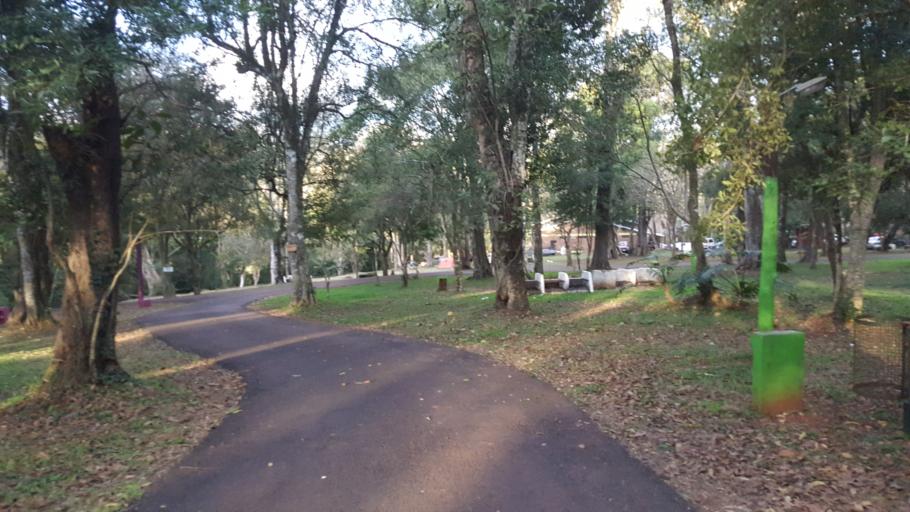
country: AR
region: Misiones
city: Puerto Leoni
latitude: -26.9991
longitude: -55.1797
